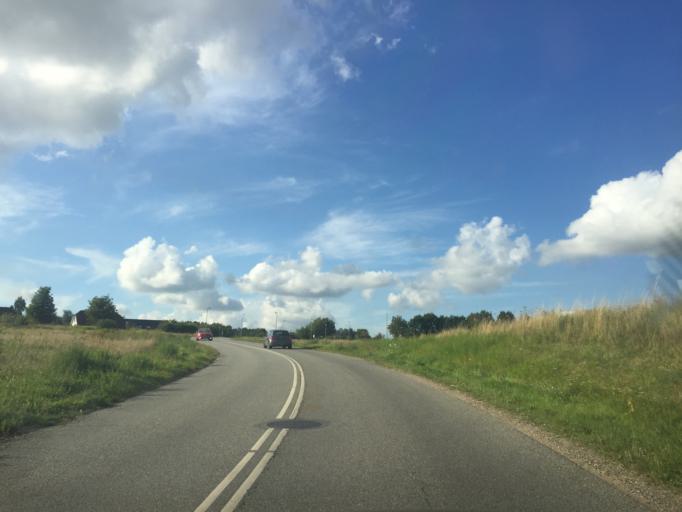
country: DK
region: Capital Region
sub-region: Egedal Kommune
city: Vekso
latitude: 55.7507
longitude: 12.2510
